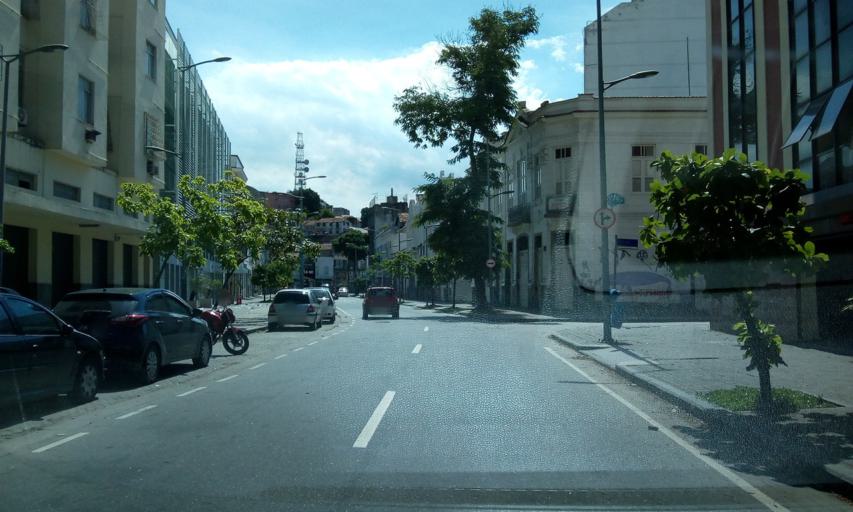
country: BR
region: Rio de Janeiro
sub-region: Rio De Janeiro
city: Rio de Janeiro
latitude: -22.8974
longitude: -43.1857
